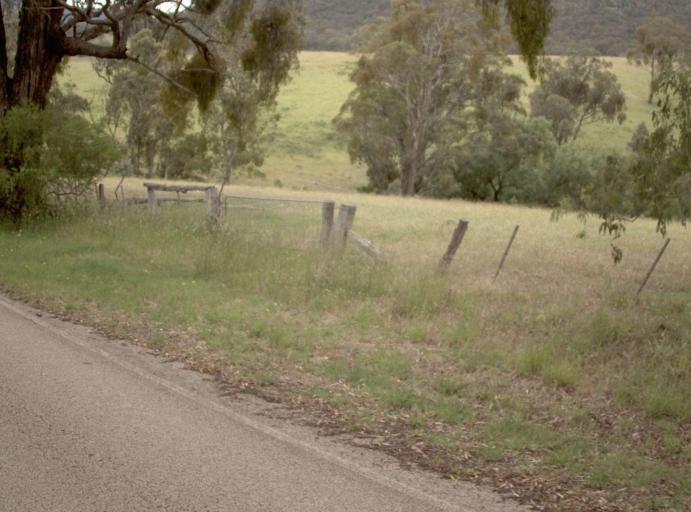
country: AU
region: Victoria
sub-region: East Gippsland
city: Bairnsdale
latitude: -37.5549
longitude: 147.1973
